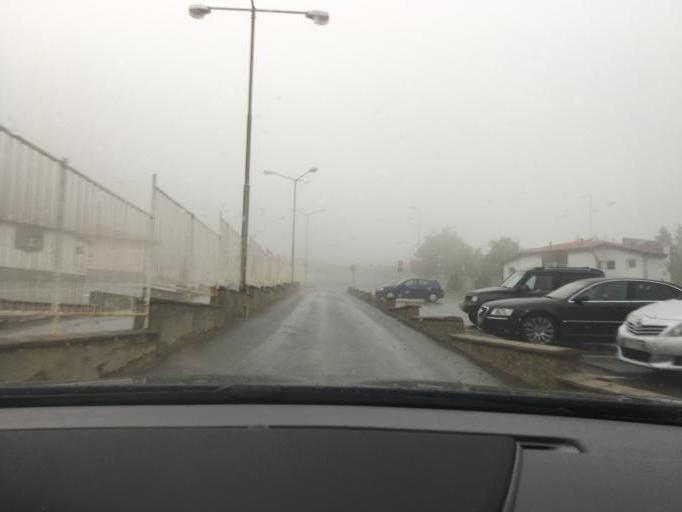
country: MK
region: Kriva Palanka
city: Kriva Palanka
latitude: 42.2190
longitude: 22.4623
